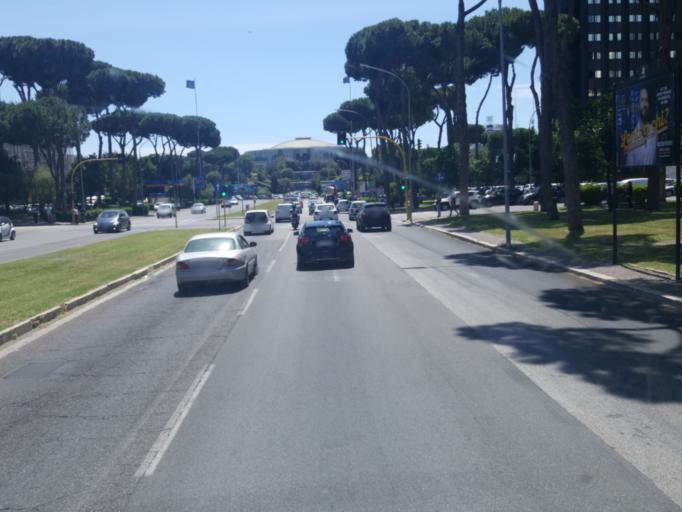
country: IT
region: Latium
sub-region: Citta metropolitana di Roma Capitale
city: Selcetta
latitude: 41.8315
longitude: 12.4695
